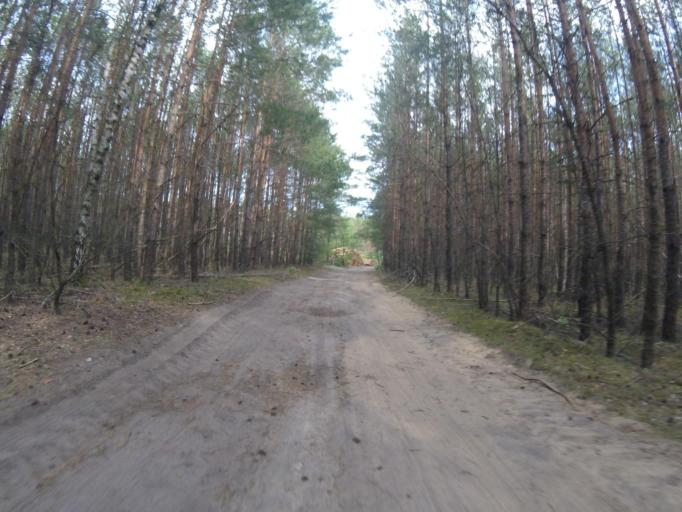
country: DE
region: Brandenburg
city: Wildau
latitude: 52.3165
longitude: 13.7378
